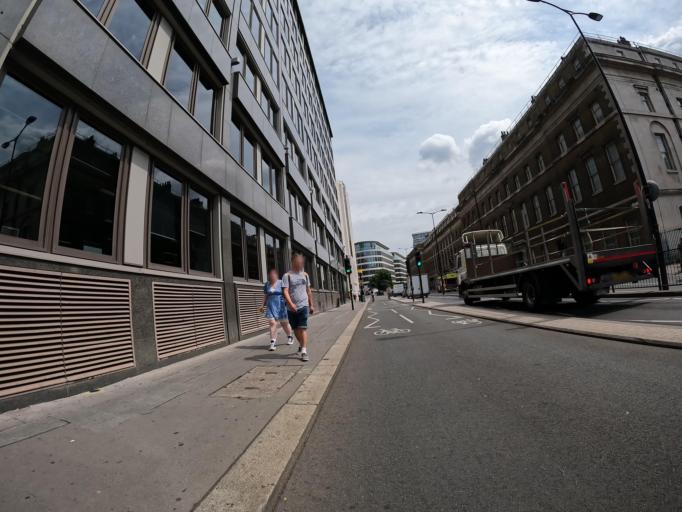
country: GB
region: England
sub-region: Greater London
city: Hendon
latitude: 51.6120
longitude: -0.1798
